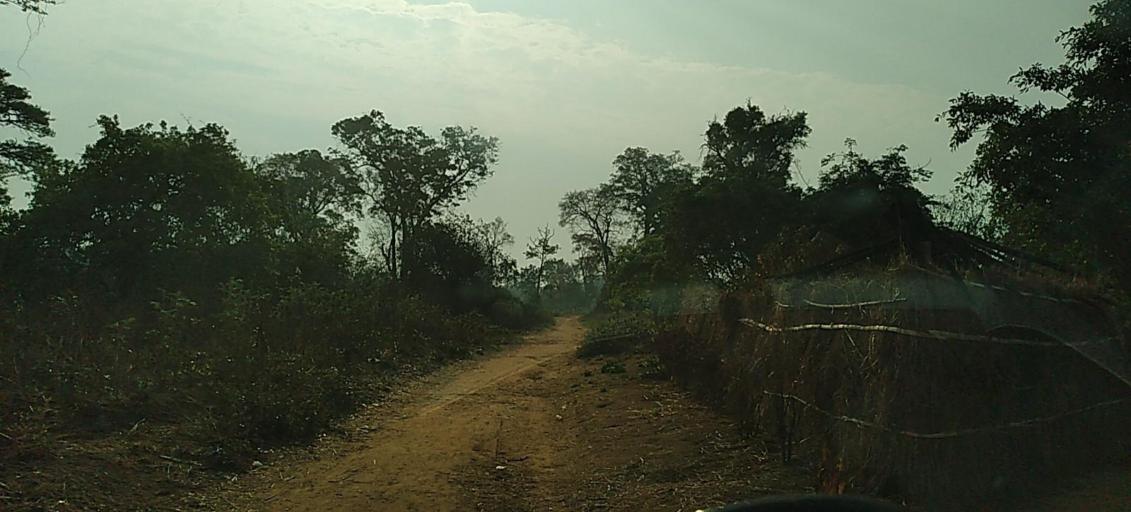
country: ZM
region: North-Western
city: Solwezi
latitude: -12.3529
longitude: 26.5367
